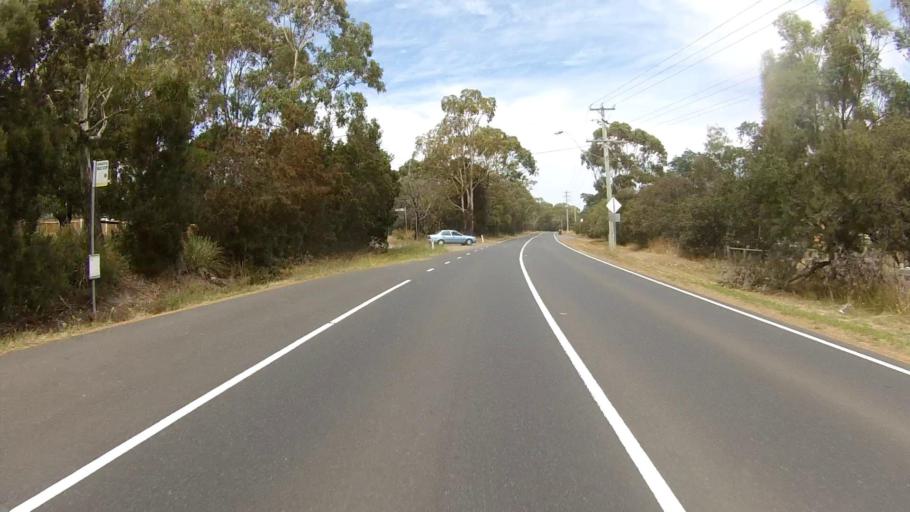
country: AU
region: Tasmania
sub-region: Clarence
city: Acton Park
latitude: -42.8746
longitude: 147.4829
